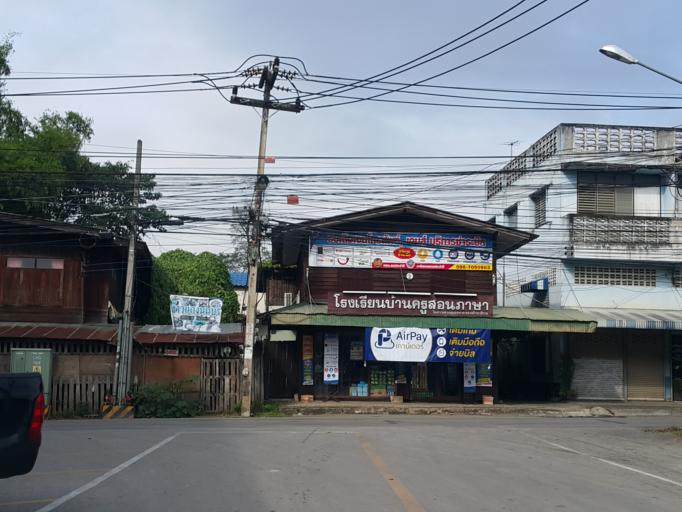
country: TH
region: Lampang
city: Lampang
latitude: 18.2953
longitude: 99.5026
